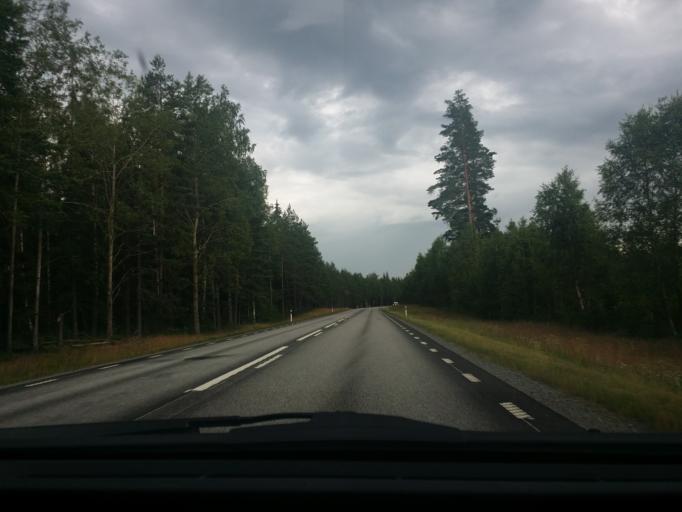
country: SE
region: OErebro
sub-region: Nora Kommun
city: Nora
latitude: 59.4770
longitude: 15.1117
